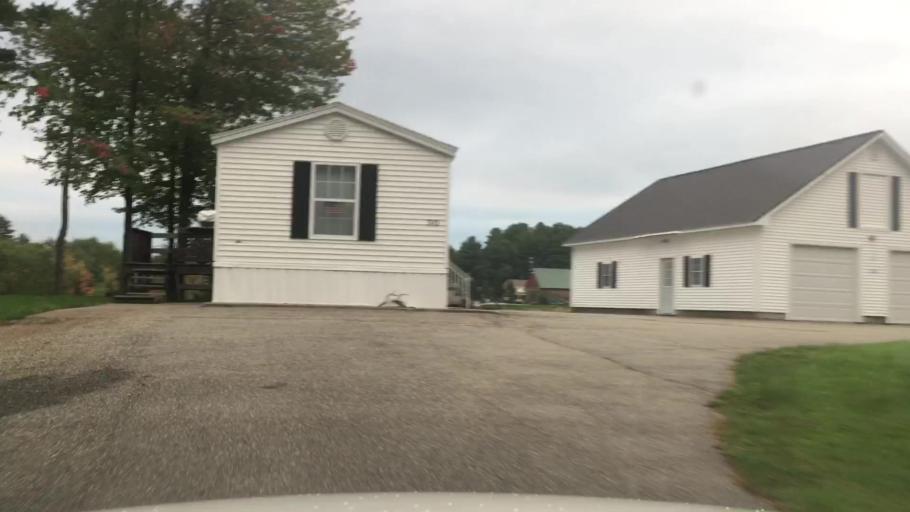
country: US
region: Maine
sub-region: York County
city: Buxton
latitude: 43.6445
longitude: -70.5244
